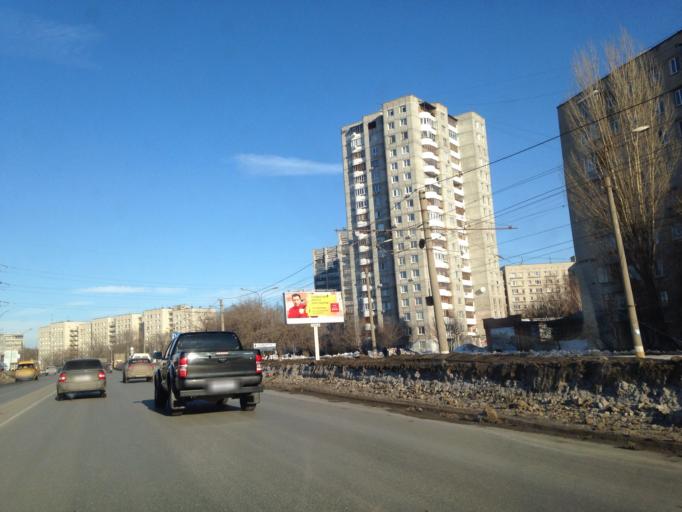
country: RU
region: Ulyanovsk
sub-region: Ulyanovskiy Rayon
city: Ulyanovsk
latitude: 54.3139
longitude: 48.3544
